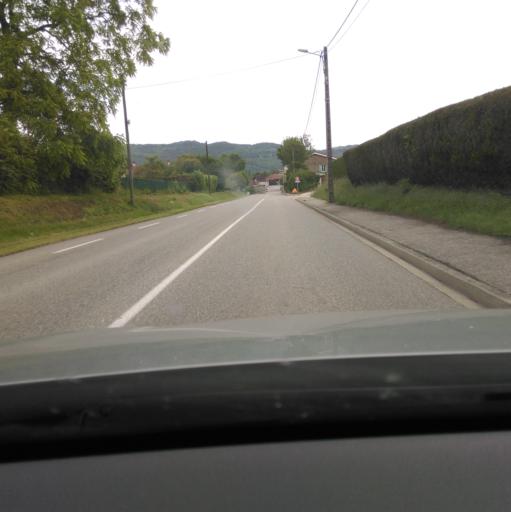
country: FR
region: Rhone-Alpes
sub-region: Departement de l'Ain
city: Izernore
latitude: 46.1858
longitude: 5.5460
